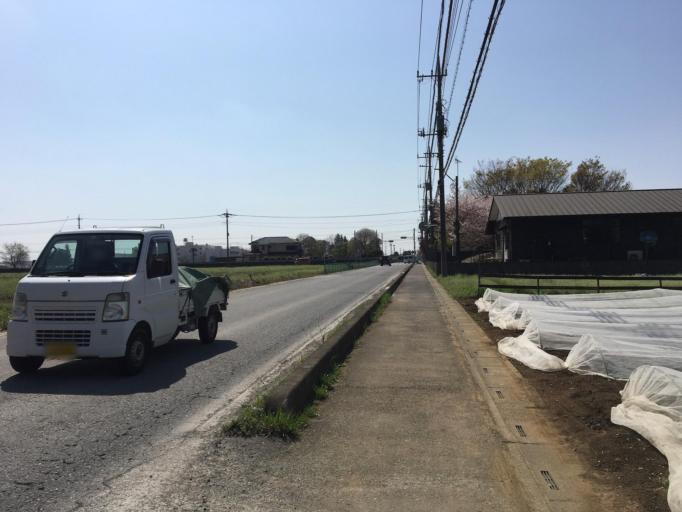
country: JP
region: Saitama
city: Sakado
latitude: 35.9140
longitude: 139.3634
